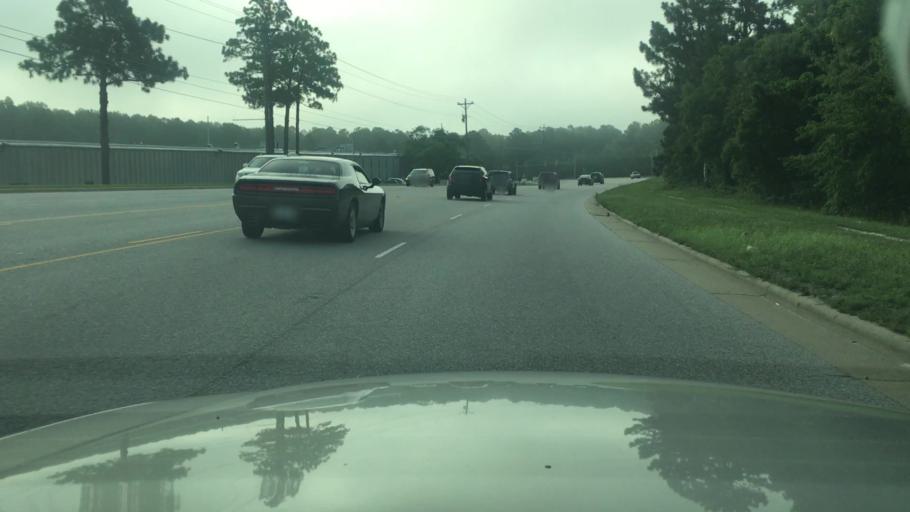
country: US
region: North Carolina
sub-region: Cumberland County
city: Hope Mills
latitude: 35.0014
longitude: -78.9078
